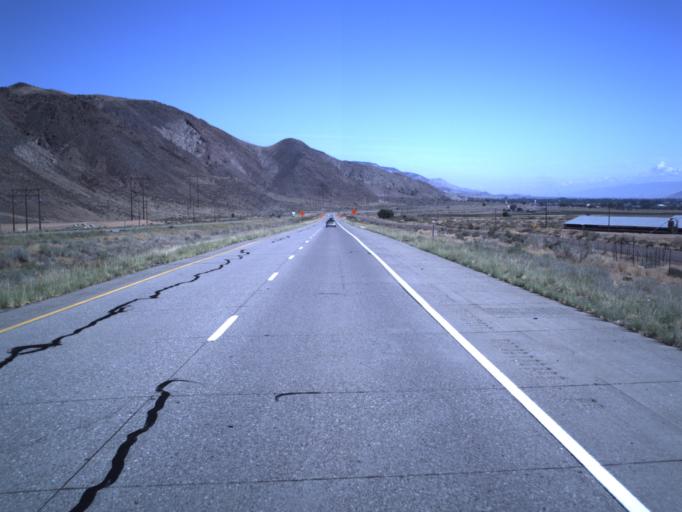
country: US
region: Utah
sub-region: Sevier County
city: Richfield
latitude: 38.7148
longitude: -112.1349
